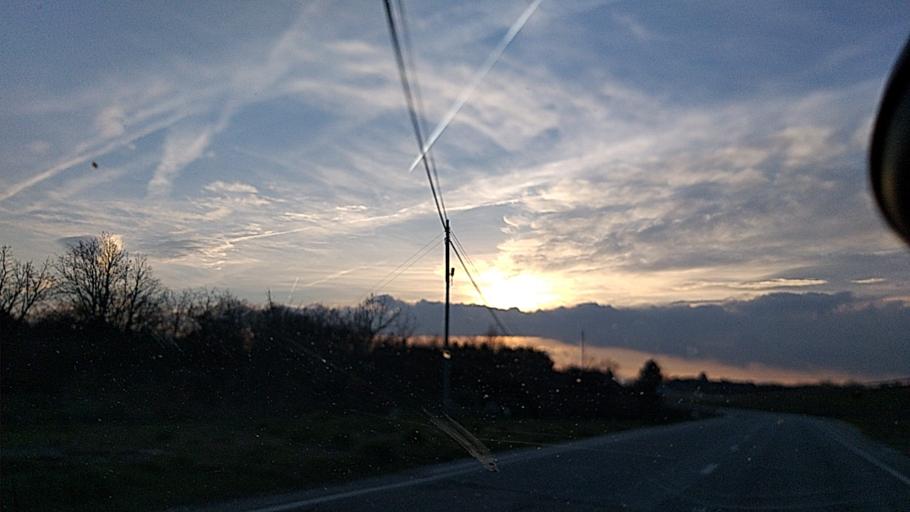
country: PT
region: Guarda
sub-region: Guarda
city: Sequeira
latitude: 40.5814
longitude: -7.1578
